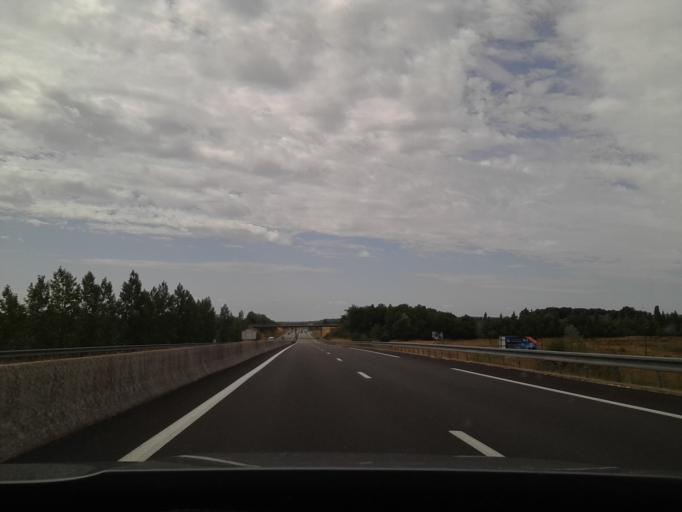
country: FR
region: Pays de la Loire
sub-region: Departement de la Sarthe
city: Beaumont-sur-Sarthe
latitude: 48.2020
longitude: 0.1744
